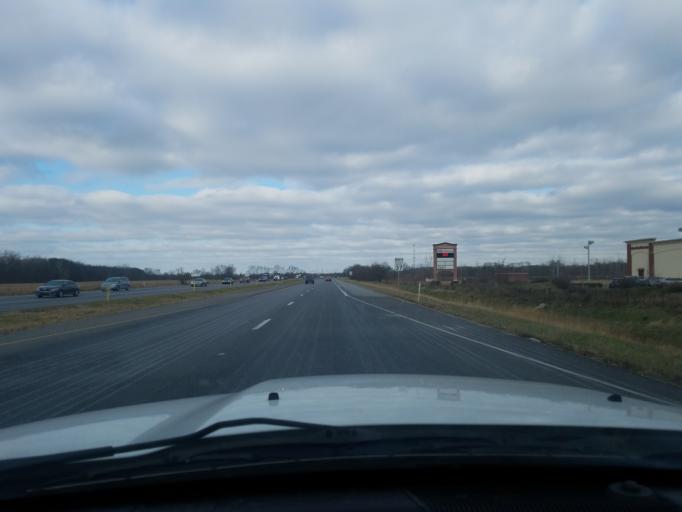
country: US
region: Indiana
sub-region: Johnson County
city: Waterloo
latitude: 39.6196
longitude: -86.2124
